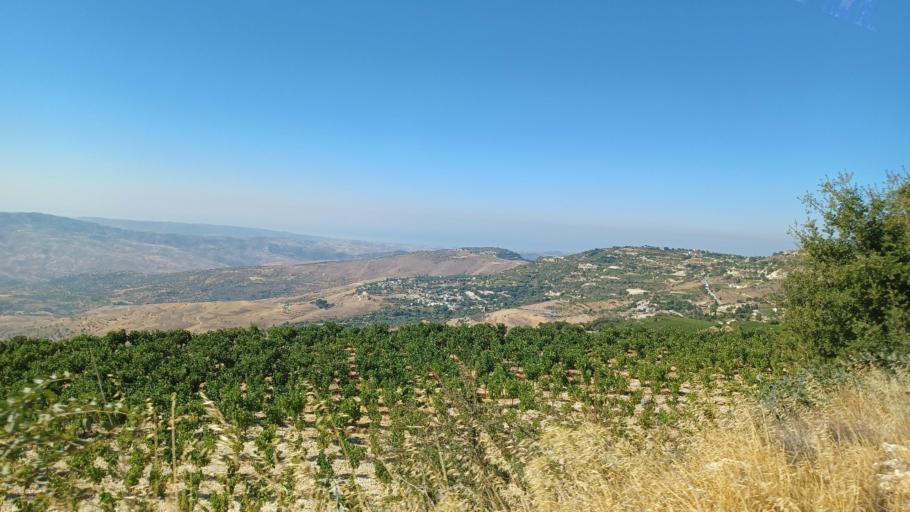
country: CY
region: Limassol
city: Pachna
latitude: 34.8986
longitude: 32.6393
